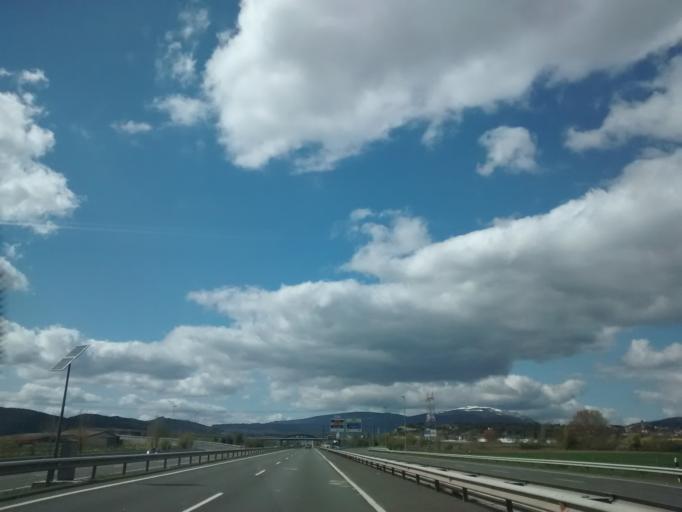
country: ES
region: Basque Country
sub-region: Provincia de Alava
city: Gasteiz / Vitoria
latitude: 42.8996
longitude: -2.7069
